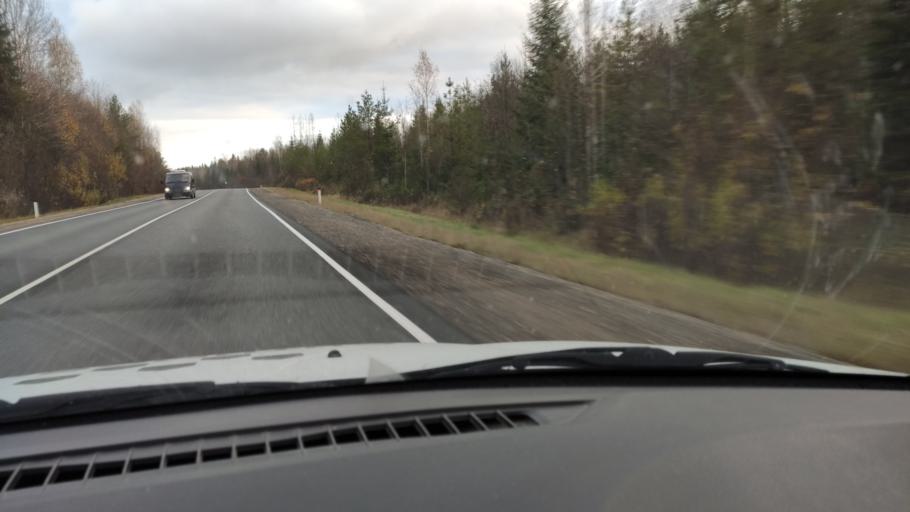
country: RU
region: Kirov
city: Omutninsk
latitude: 58.7103
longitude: 52.0983
